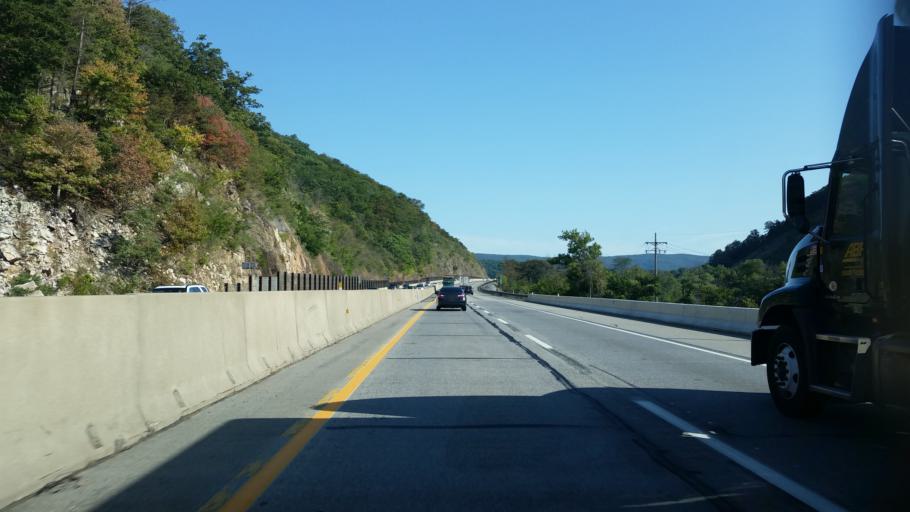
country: US
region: Pennsylvania
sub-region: Bedford County
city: Bedford
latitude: 40.0196
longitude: -78.4759
